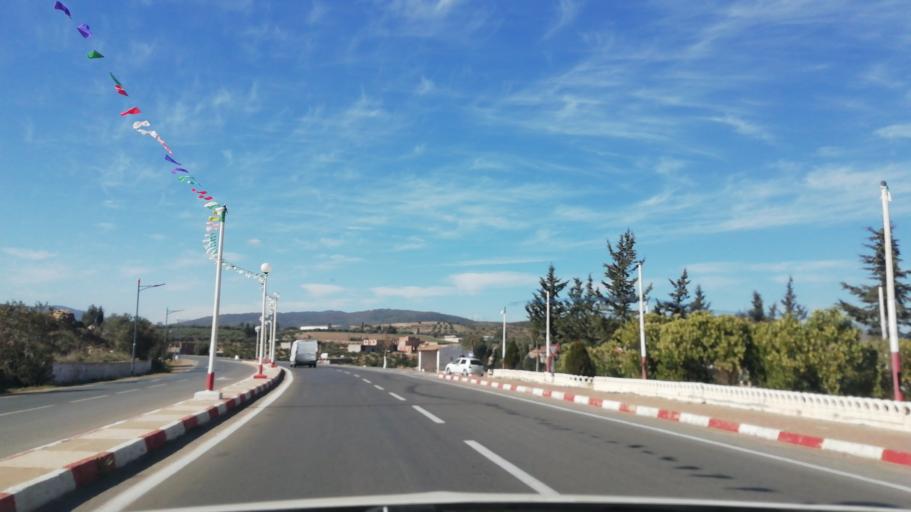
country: DZ
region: Tlemcen
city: Ouled Mimoun
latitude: 34.8706
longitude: -1.1420
